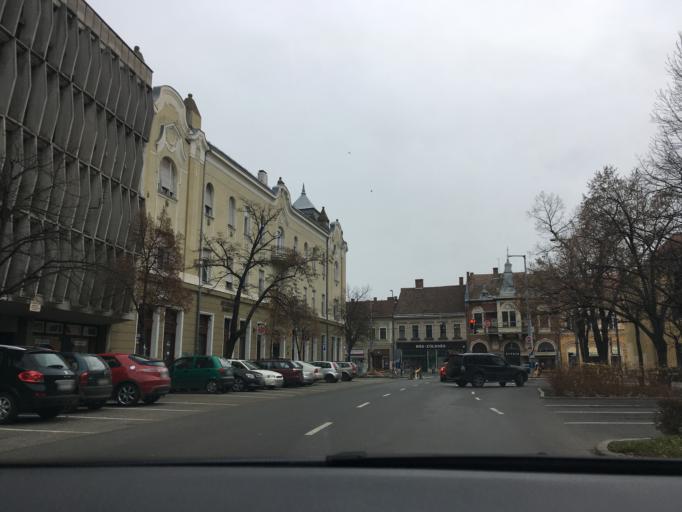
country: HU
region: Hajdu-Bihar
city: Debrecen
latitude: 47.5299
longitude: 21.6268
